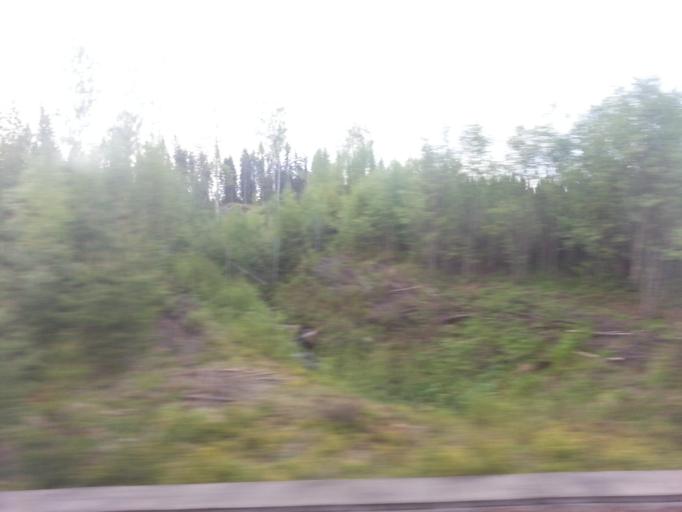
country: NO
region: Akershus
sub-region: Eidsvoll
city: Raholt
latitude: 60.2682
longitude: 11.1460
